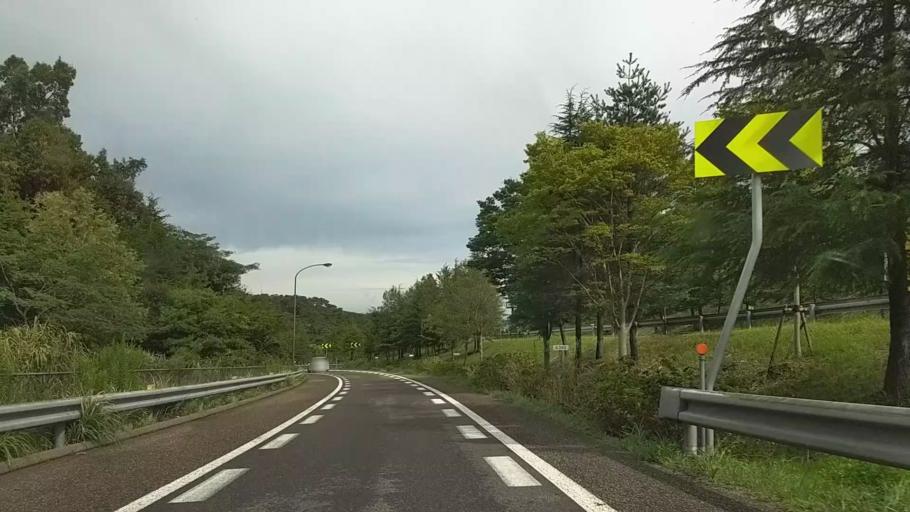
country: JP
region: Niigata
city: Joetsu
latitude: 37.1383
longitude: 138.2141
